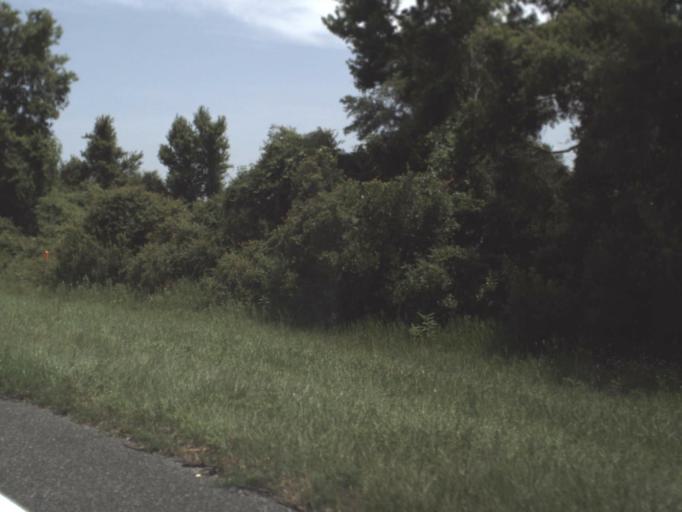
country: US
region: Florida
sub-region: Taylor County
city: Steinhatchee
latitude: 29.8283
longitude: -83.3591
